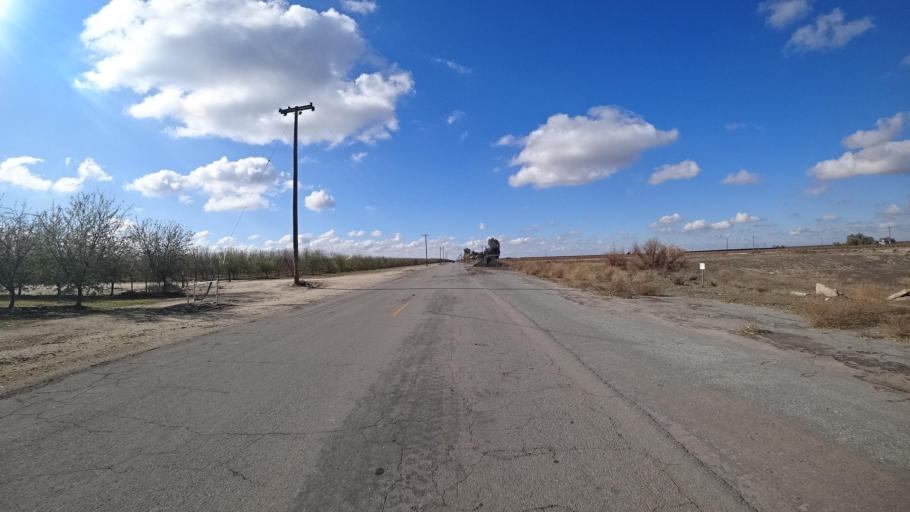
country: US
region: California
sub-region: Kern County
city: Delano
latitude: 35.7326
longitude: -119.3432
